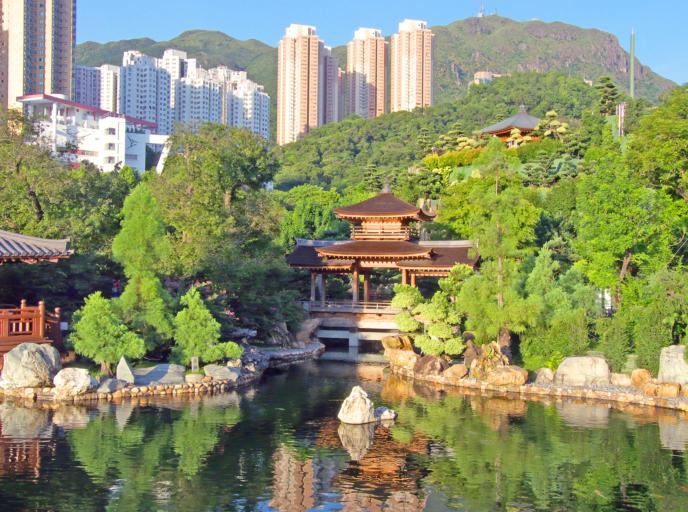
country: HK
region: Wong Tai Sin
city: Wong Tai Sin
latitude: 22.3389
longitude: 114.2049
